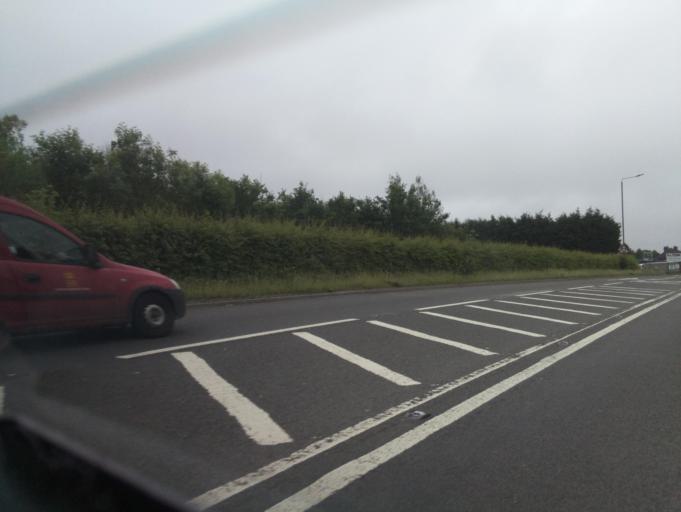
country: GB
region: England
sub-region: Derbyshire
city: Swadlincote
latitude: 52.7501
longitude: -1.5734
